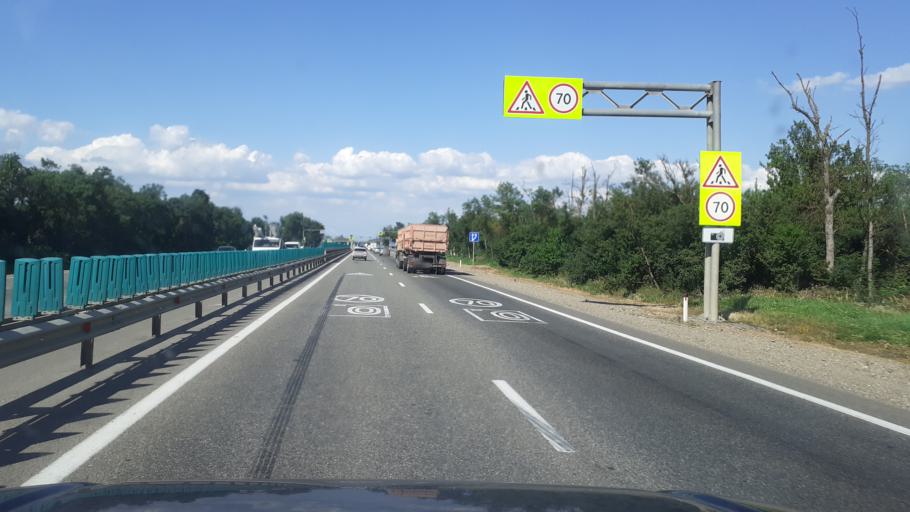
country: RU
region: Krasnodarskiy
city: Severskaya
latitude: 44.8643
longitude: 38.7523
